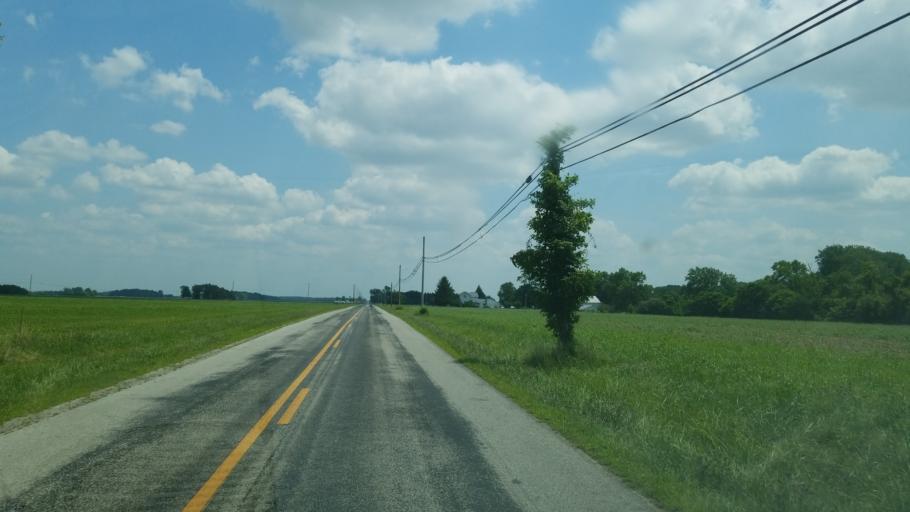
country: US
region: Ohio
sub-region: Henry County
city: Napoleon
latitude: 41.3415
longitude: -84.0811
